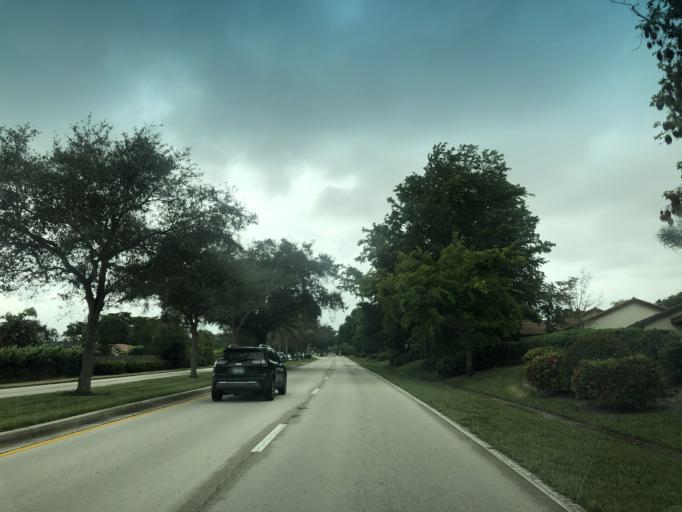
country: US
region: Florida
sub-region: Broward County
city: Margate
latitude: 26.2512
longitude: -80.2406
